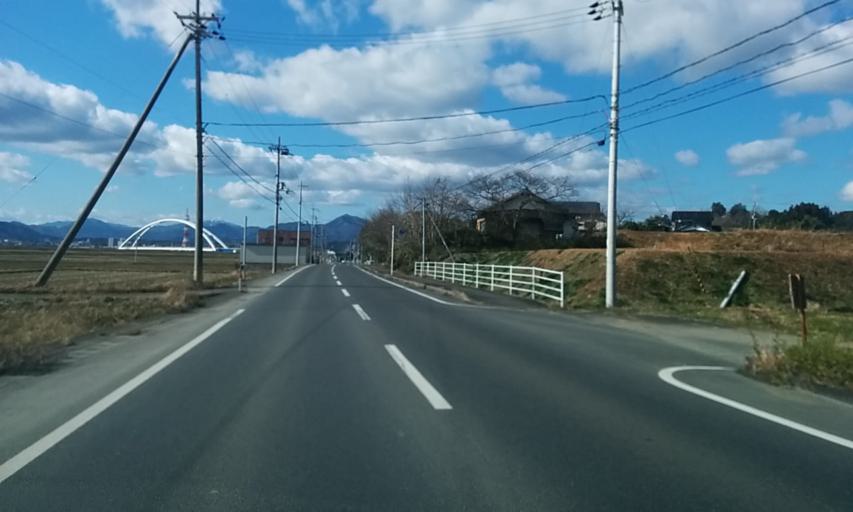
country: JP
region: Kyoto
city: Fukuchiyama
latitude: 35.3049
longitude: 135.1402
